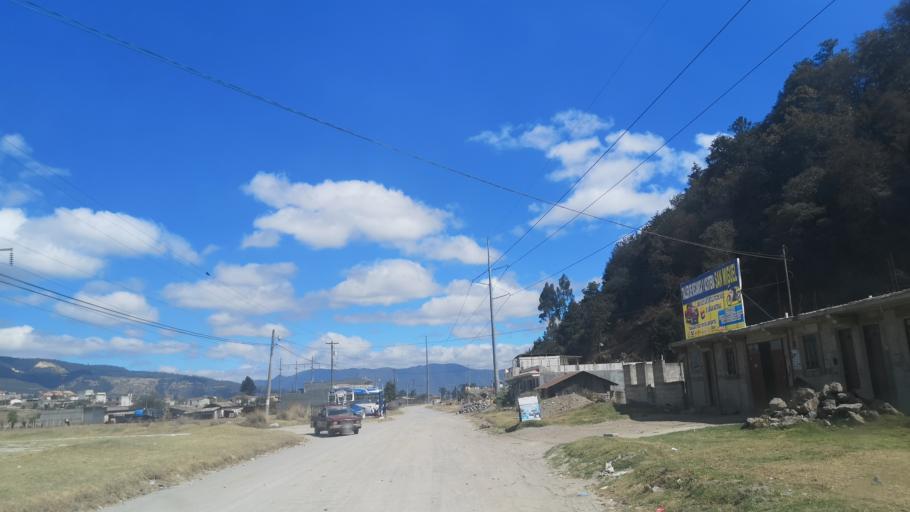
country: GT
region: Quetzaltenango
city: Almolonga
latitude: 14.7878
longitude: -91.5368
